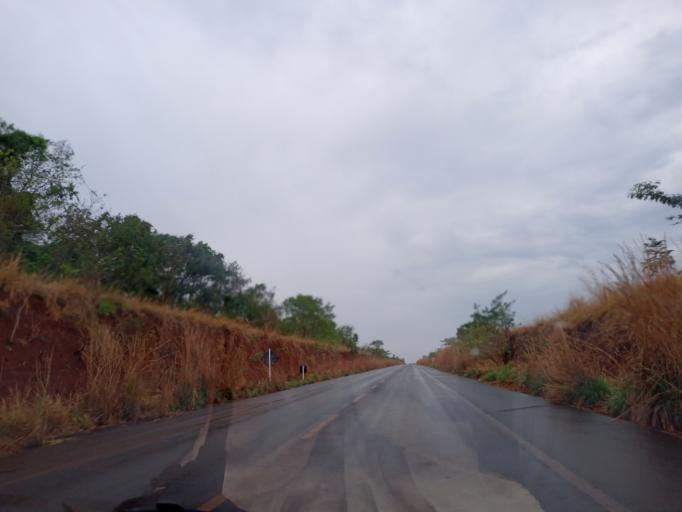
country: BR
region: Minas Gerais
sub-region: Ituiutaba
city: Ituiutaba
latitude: -19.1212
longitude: -49.5192
